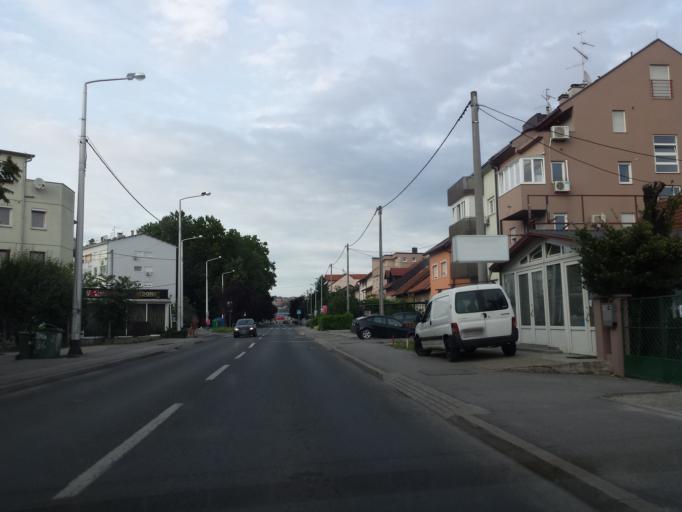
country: HR
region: Grad Zagreb
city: Jankomir
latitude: 45.8079
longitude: 15.9261
